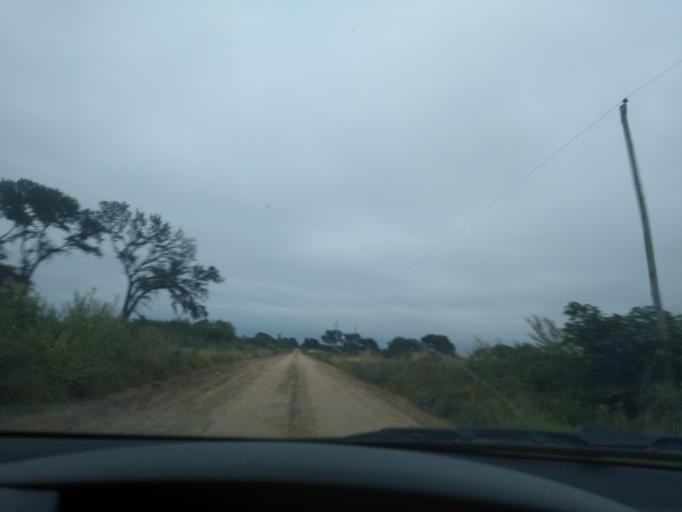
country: AR
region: Chaco
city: Colonia Benitez
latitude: -27.3633
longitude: -58.9562
